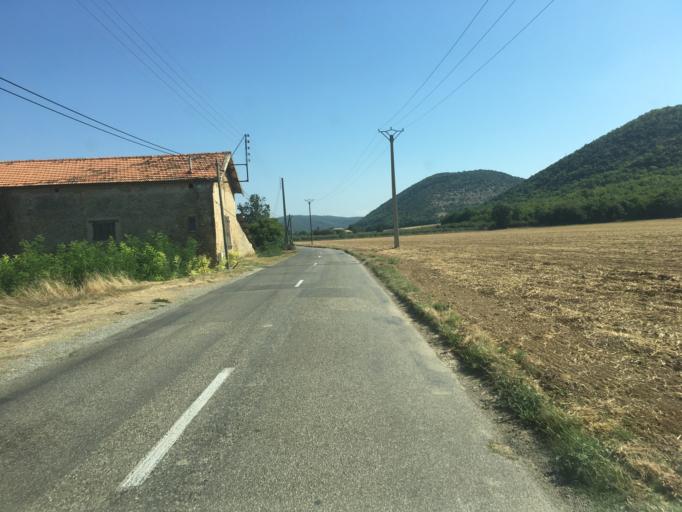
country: FR
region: Provence-Alpes-Cote d'Azur
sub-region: Departement des Alpes-de-Haute-Provence
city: Villeneuve
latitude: 43.8643
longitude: 5.8948
